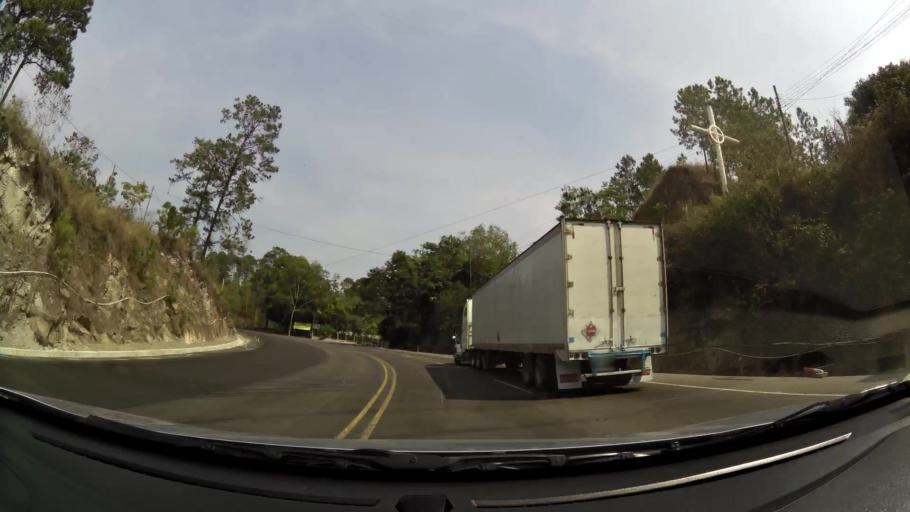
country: HN
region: Comayagua
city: Potrerillos
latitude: 14.5399
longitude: -87.8181
